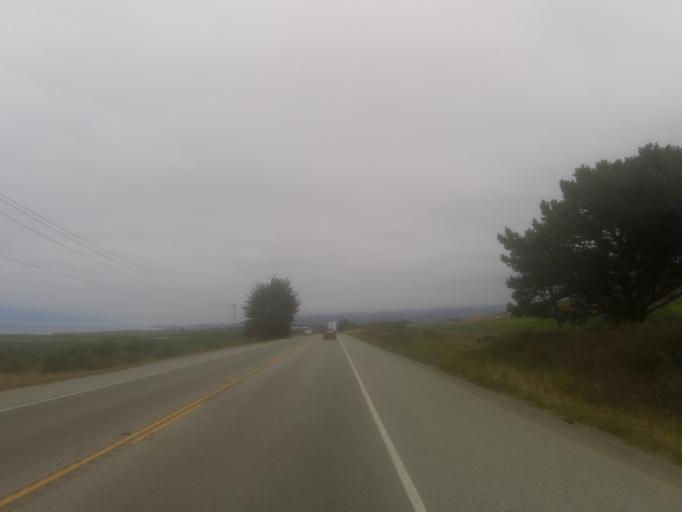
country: US
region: California
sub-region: San Mateo County
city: Half Moon Bay
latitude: 37.4094
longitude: -122.4218
